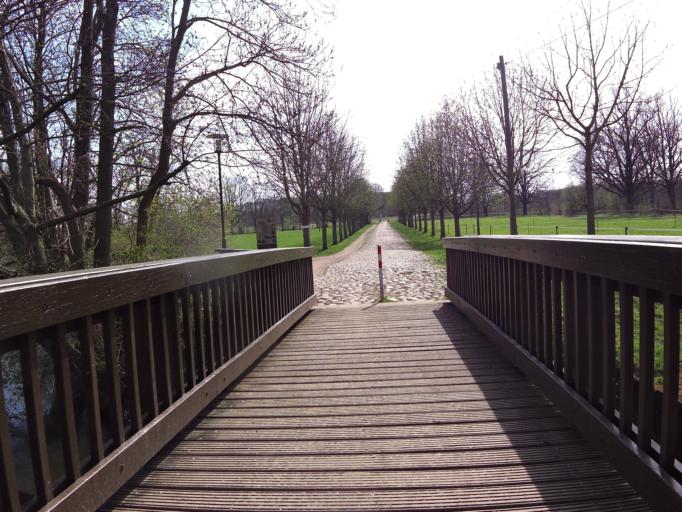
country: DE
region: Saxony
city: Schkeuditz
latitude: 51.3783
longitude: 12.2802
